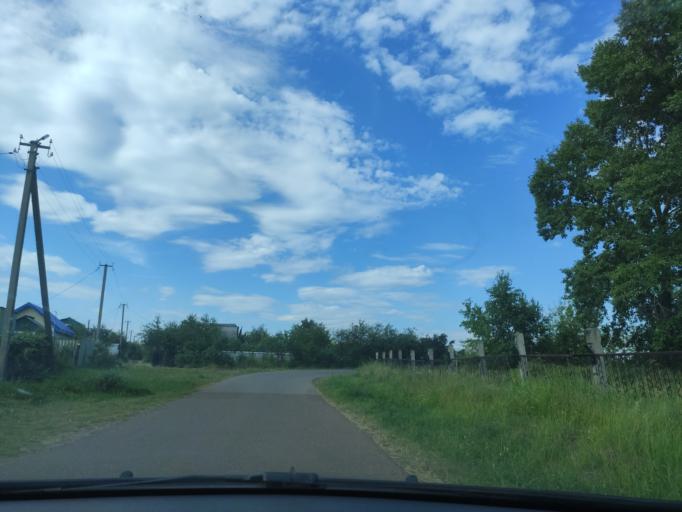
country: RU
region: Ulyanovsk
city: Cherdakly
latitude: 54.4406
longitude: 48.9051
